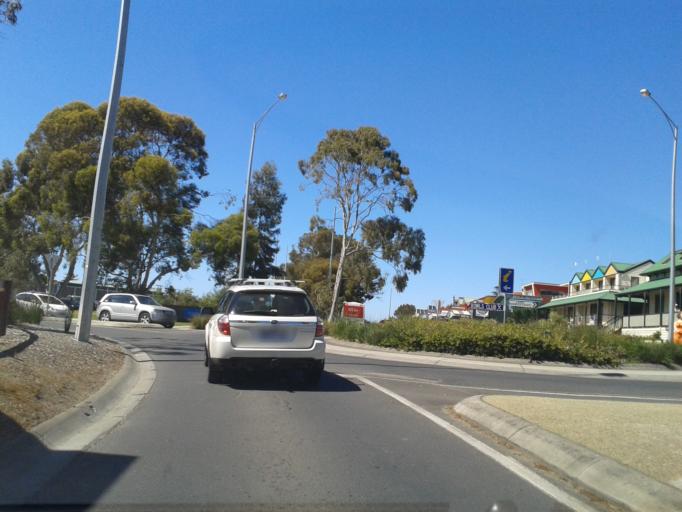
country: AU
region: Victoria
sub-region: Surf Coast
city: Anglesea
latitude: -38.5366
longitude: 143.9738
